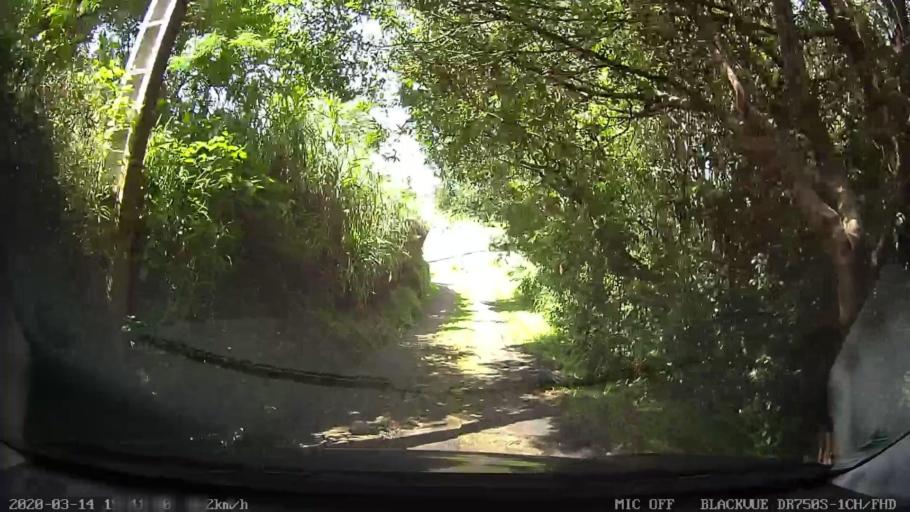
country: RE
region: Reunion
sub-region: Reunion
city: Sainte-Marie
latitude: -20.9470
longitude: 55.5258
